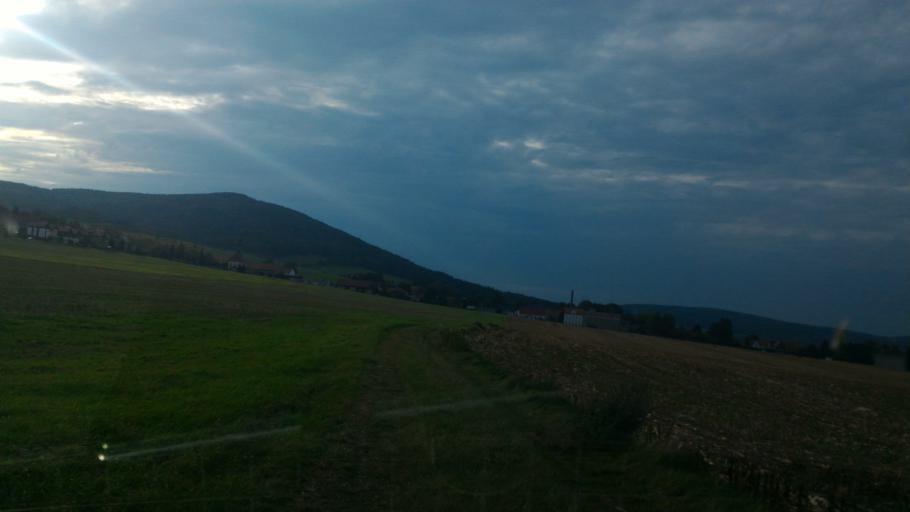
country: DE
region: Saxony
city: Grossschonau
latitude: 50.8704
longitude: 14.6616
